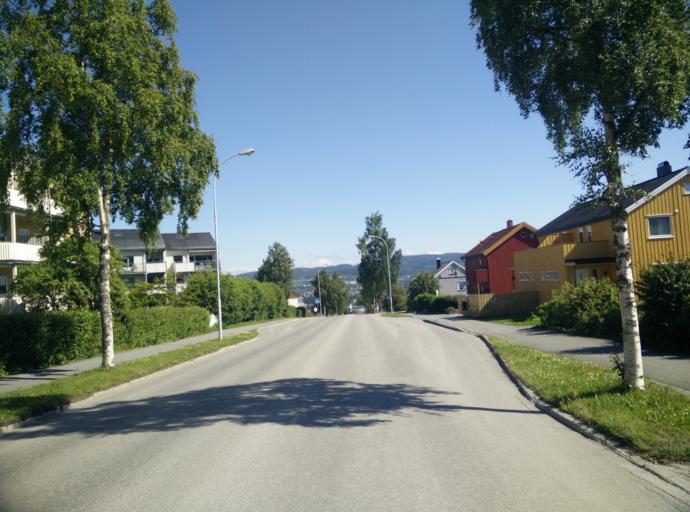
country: NO
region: Sor-Trondelag
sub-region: Trondheim
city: Trondheim
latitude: 63.4160
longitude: 10.3614
